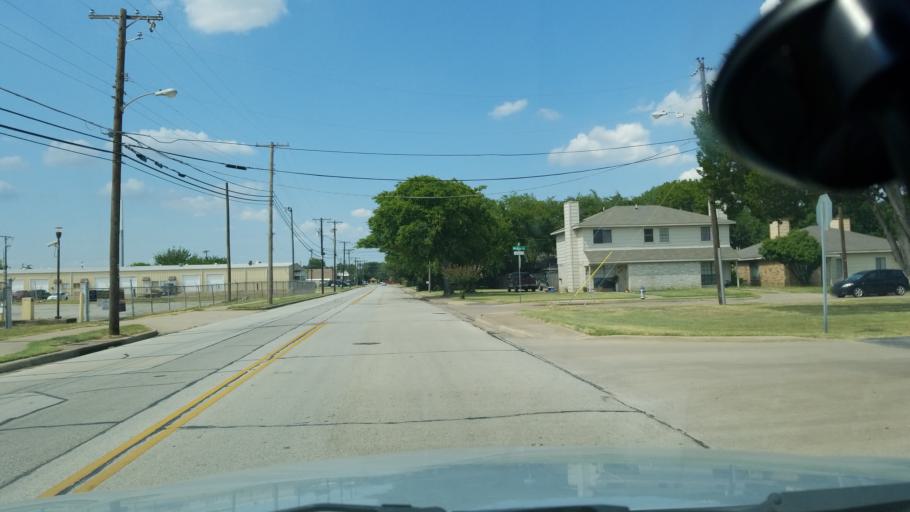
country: US
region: Texas
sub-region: Dallas County
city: Irving
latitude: 32.8184
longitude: -96.9894
